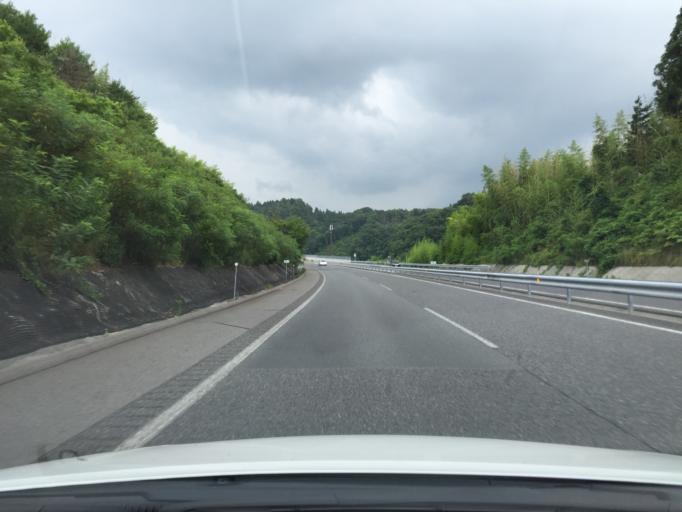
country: JP
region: Fukushima
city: Funehikimachi-funehiki
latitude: 37.2568
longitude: 140.6501
